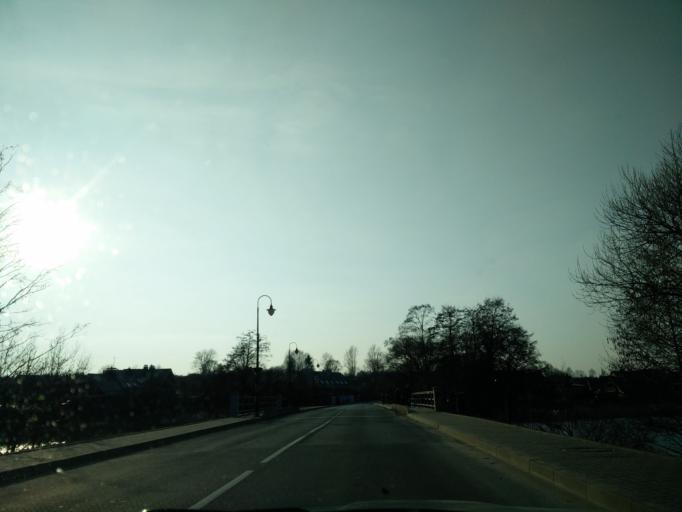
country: LT
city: Trakai
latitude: 54.6499
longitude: 24.9276
